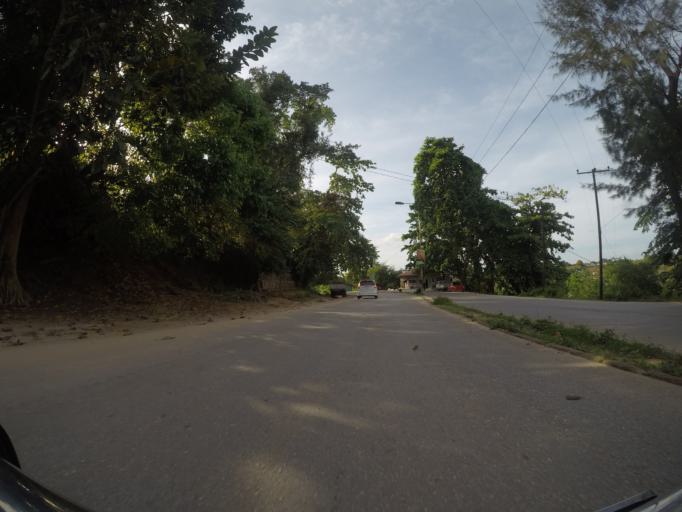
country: TZ
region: Pemba South
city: Chake Chake
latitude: -5.2399
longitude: 39.7711
